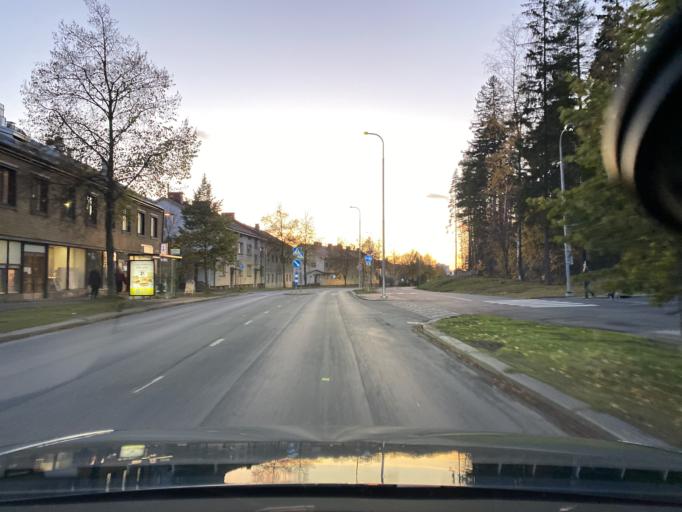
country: FI
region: Pirkanmaa
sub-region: Tampere
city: Tampere
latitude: 61.4703
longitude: 23.7422
